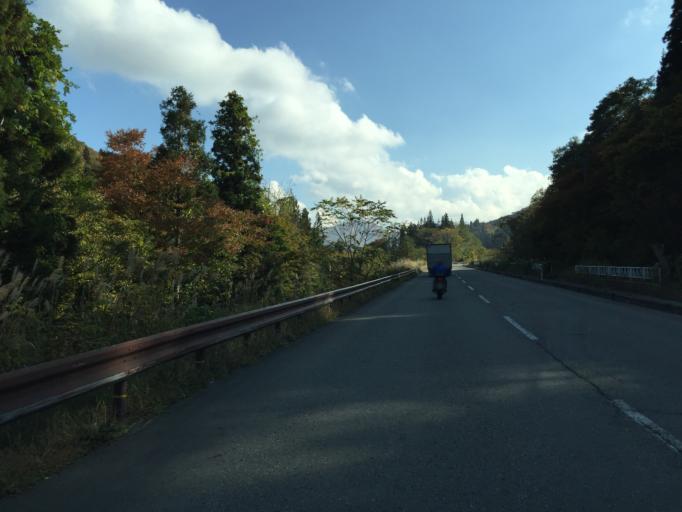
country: JP
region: Yamagata
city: Yonezawa
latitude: 37.8595
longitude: 139.9886
